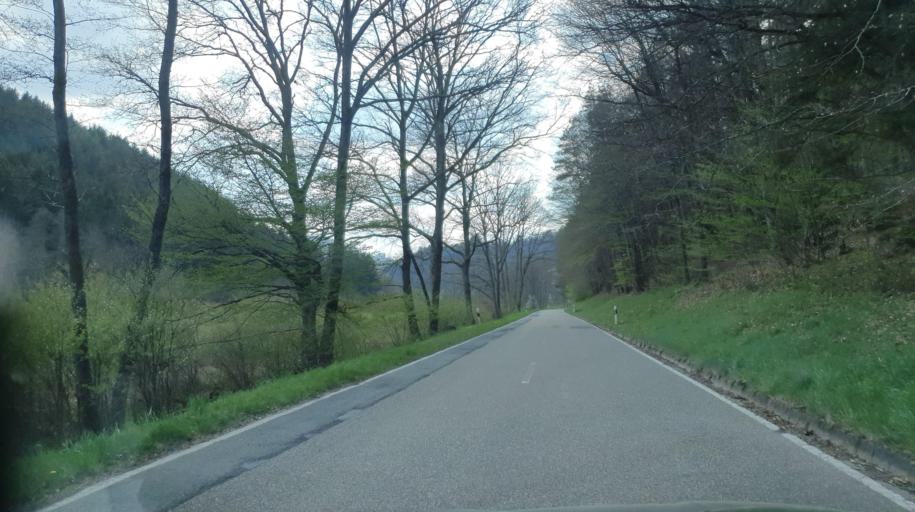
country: DE
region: Rheinland-Pfalz
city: Clausen
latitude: 49.2748
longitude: 7.7042
